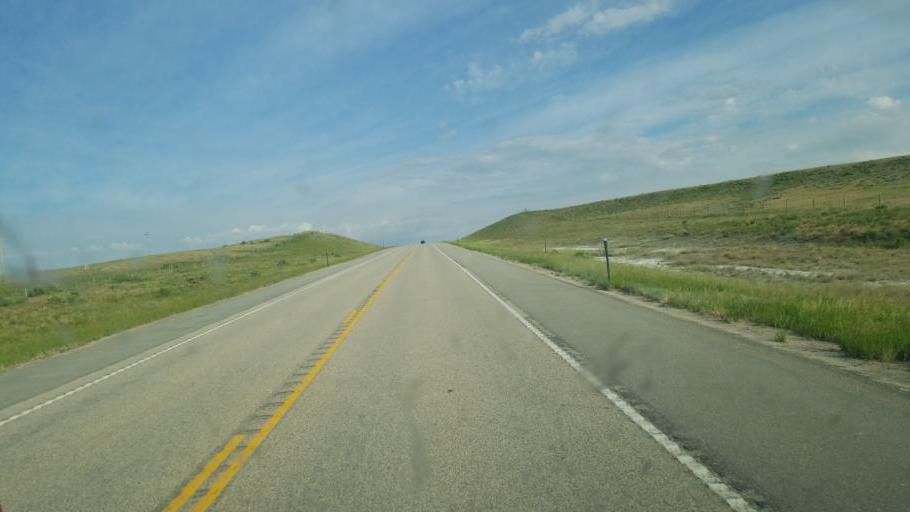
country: US
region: Wyoming
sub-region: Natrona County
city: Mills
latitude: 43.0347
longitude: -107.0231
